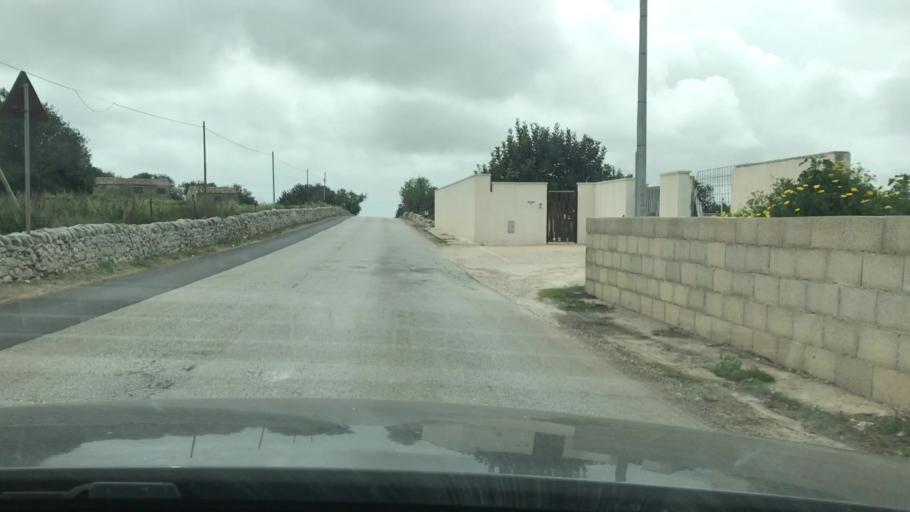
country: IT
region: Sicily
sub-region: Ragusa
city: Modica
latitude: 36.8215
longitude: 14.7470
